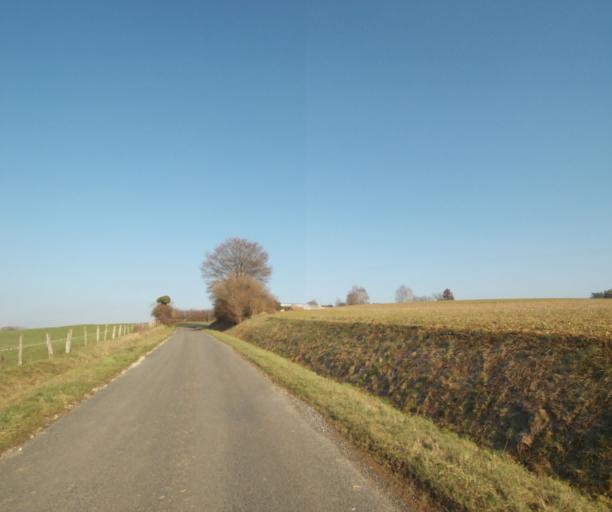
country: FR
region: Champagne-Ardenne
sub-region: Departement de la Haute-Marne
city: Wassy
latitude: 48.5216
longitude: 4.9902
